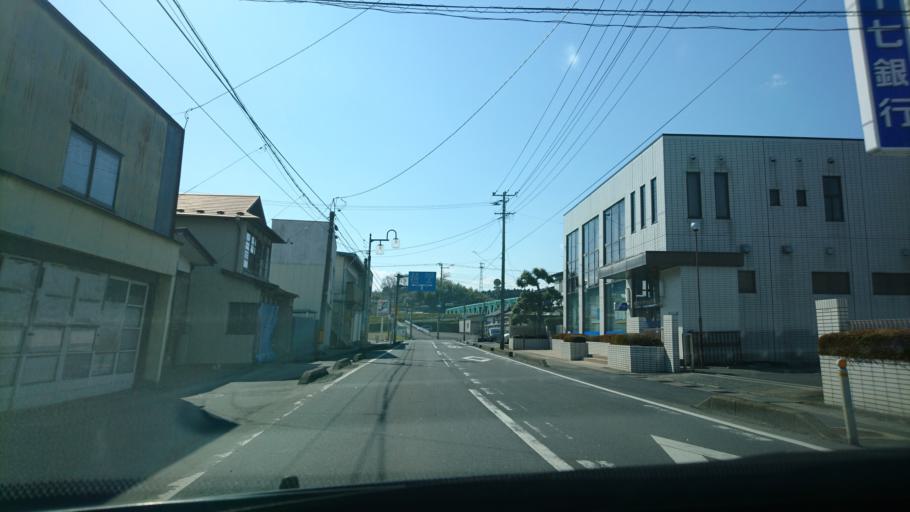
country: JP
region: Miyagi
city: Wakuya
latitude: 38.7062
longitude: 141.2894
